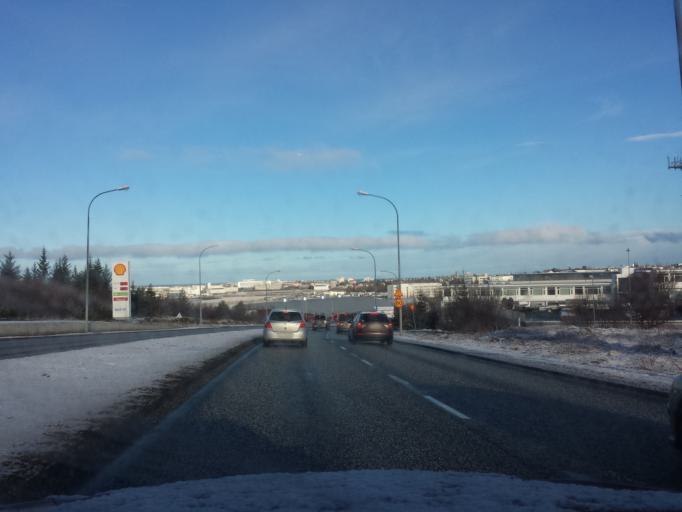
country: IS
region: Capital Region
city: Kopavogur
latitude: 64.1314
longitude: -21.9176
